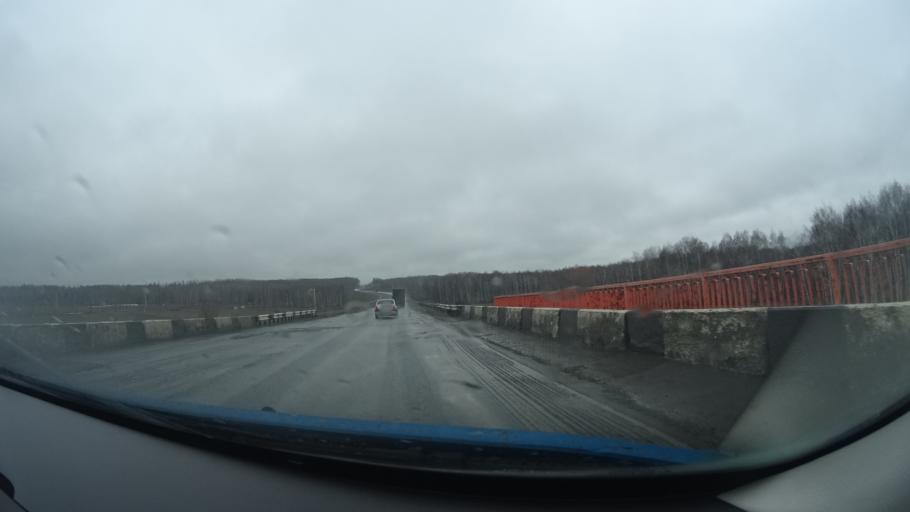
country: RU
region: Bashkortostan
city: Kandry
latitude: 54.5994
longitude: 54.2891
